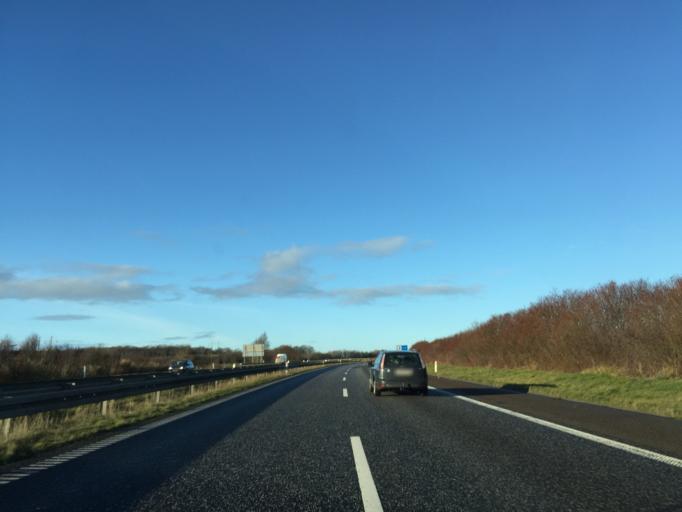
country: DK
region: South Denmark
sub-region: Fredericia Kommune
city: Taulov
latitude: 55.5940
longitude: 9.5952
